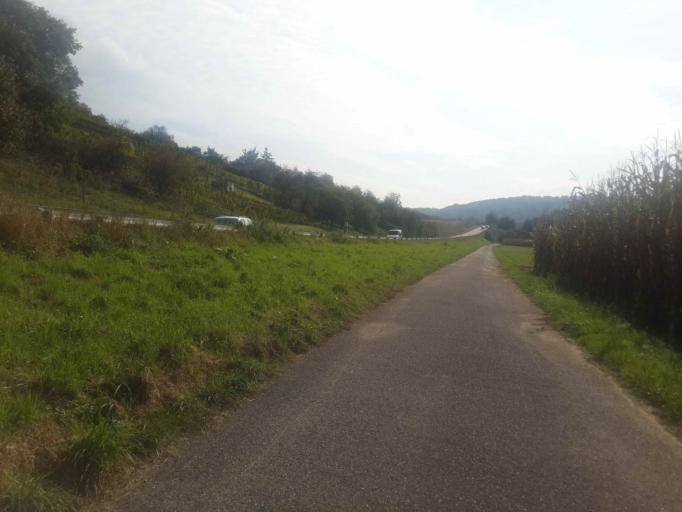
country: DE
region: Baden-Wuerttemberg
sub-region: Regierungsbezirk Stuttgart
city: Neudenau
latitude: 49.3011
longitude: 9.3155
